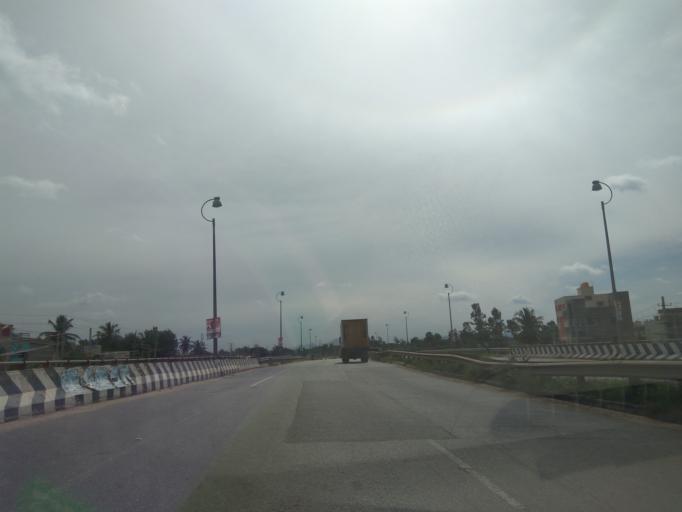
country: IN
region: Karnataka
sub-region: Bangalore Rural
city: Dasarahalli
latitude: 13.1327
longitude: 77.9295
